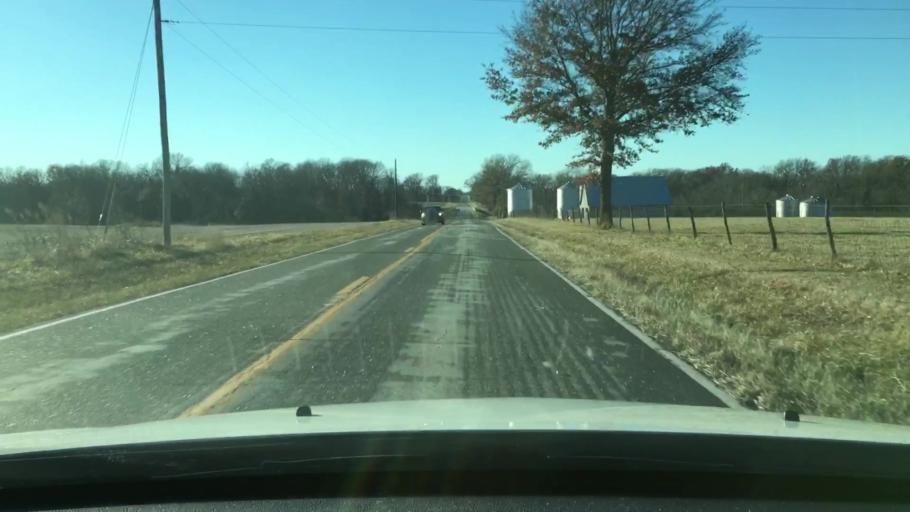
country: US
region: Missouri
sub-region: Audrain County
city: Mexico
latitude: 39.2816
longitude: -91.7112
